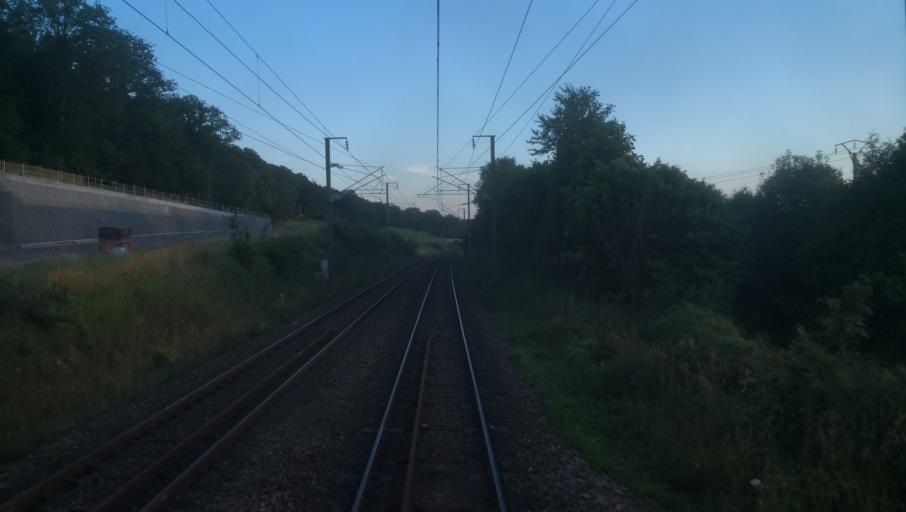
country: FR
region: Haute-Normandie
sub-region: Departement de l'Eure
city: Arnieres-sur-Iton
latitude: 49.0039
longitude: 1.1131
